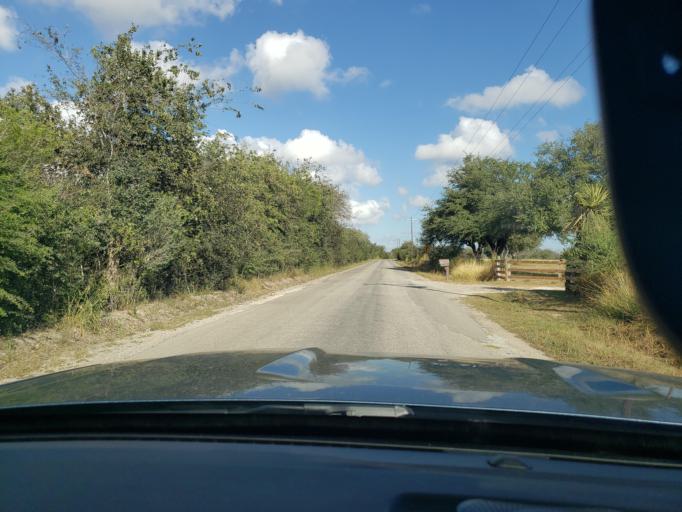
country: US
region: Texas
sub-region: Bee County
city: Beeville
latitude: 28.4453
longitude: -97.7157
